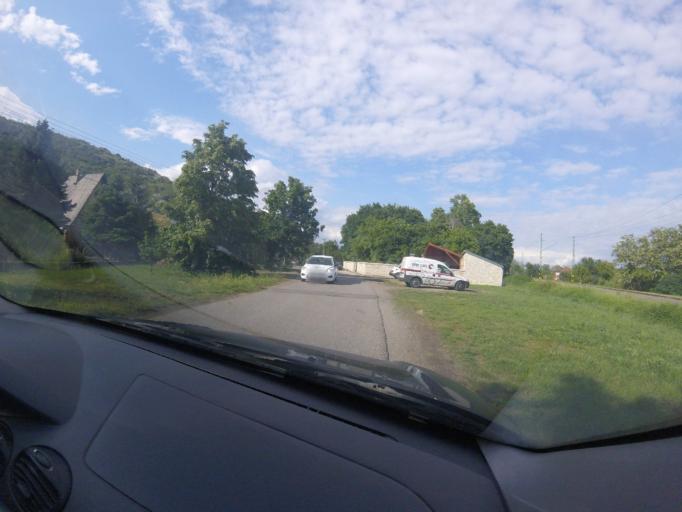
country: HU
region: Borsod-Abauj-Zemplen
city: Tokaj
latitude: 48.1142
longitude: 21.4082
